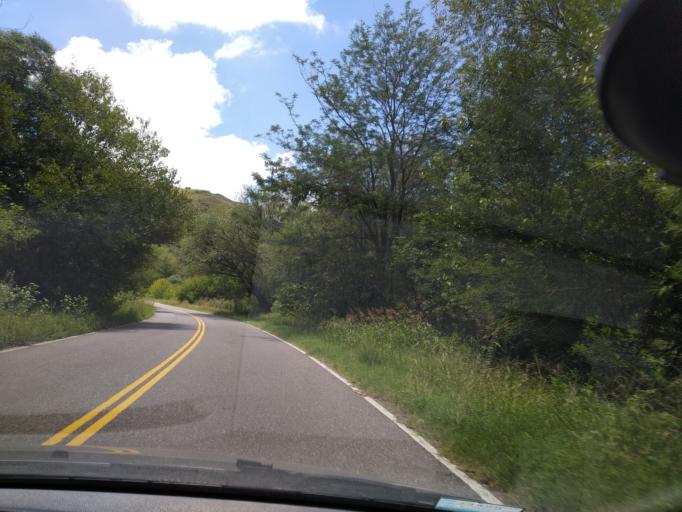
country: AR
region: Cordoba
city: Cuesta Blanca
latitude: -31.6053
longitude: -64.5550
